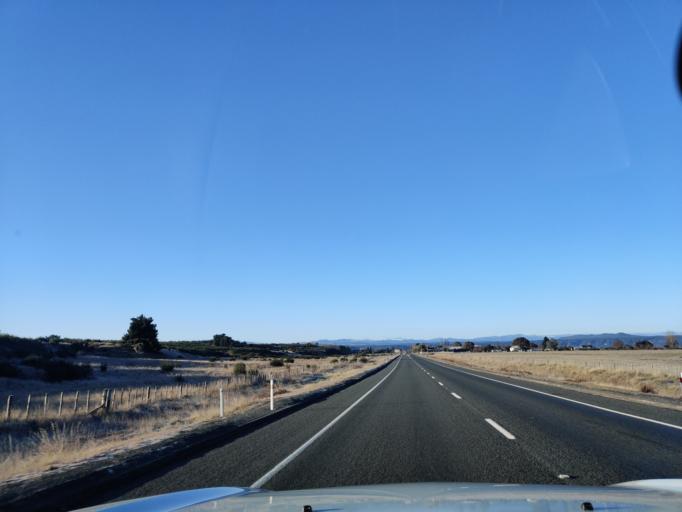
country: NZ
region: Waikato
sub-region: Taupo District
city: Taupo
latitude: -38.7468
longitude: 176.0736
